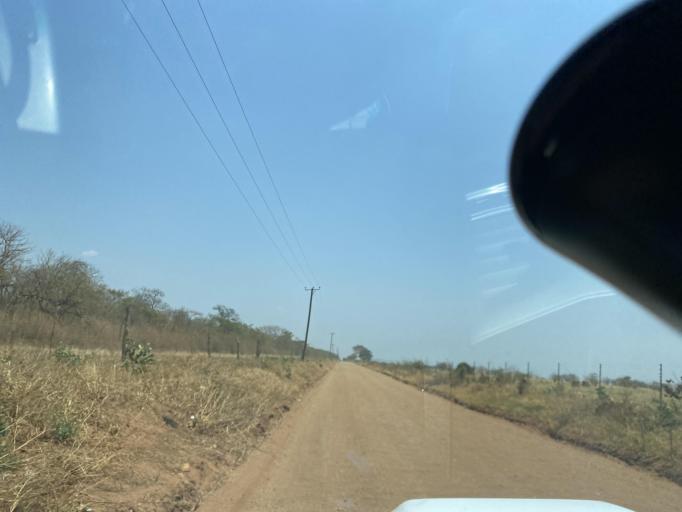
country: ZM
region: Lusaka
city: Lusaka
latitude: -15.4368
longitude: 28.0697
